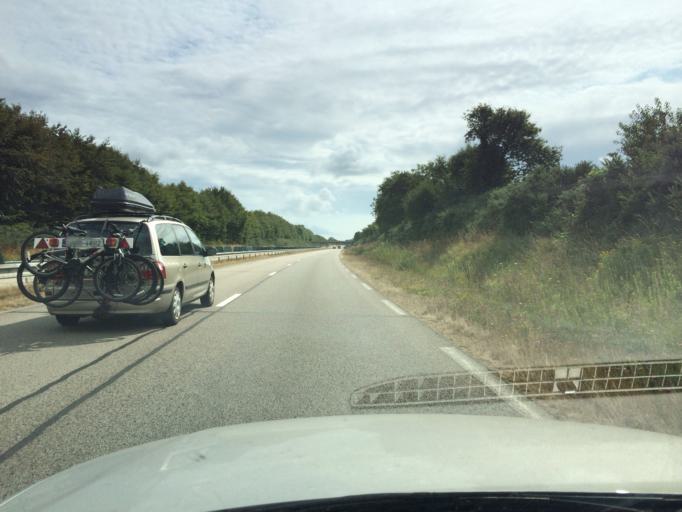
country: FR
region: Lower Normandy
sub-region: Departement de la Manche
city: Valognes
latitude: 49.4983
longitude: -1.4588
